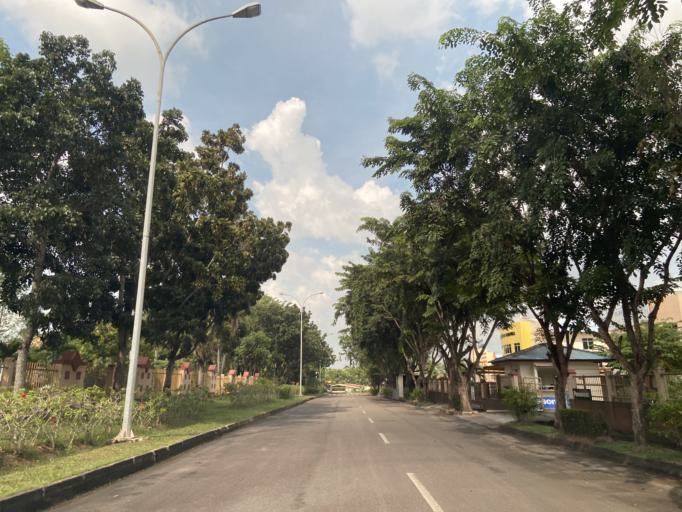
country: SG
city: Singapore
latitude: 1.1050
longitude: 104.0705
